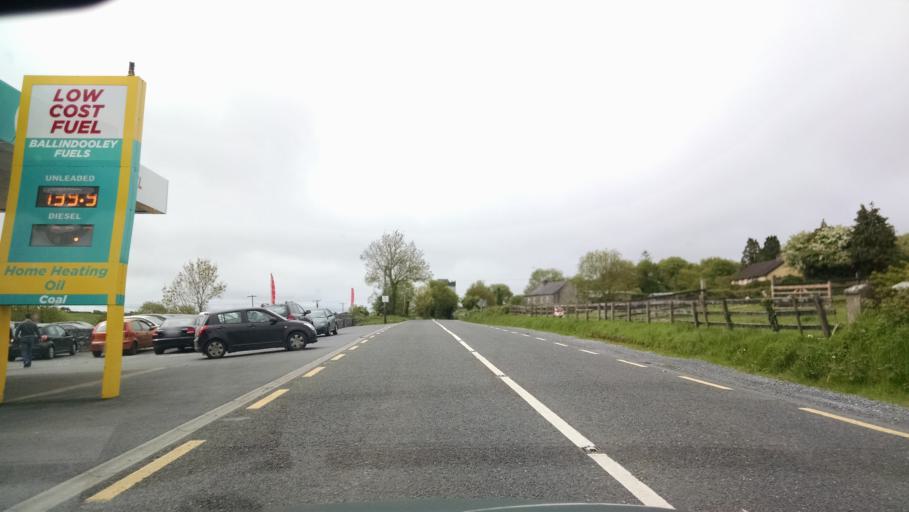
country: IE
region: Connaught
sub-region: County Galway
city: Gaillimh
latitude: 53.3111
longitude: -9.0256
